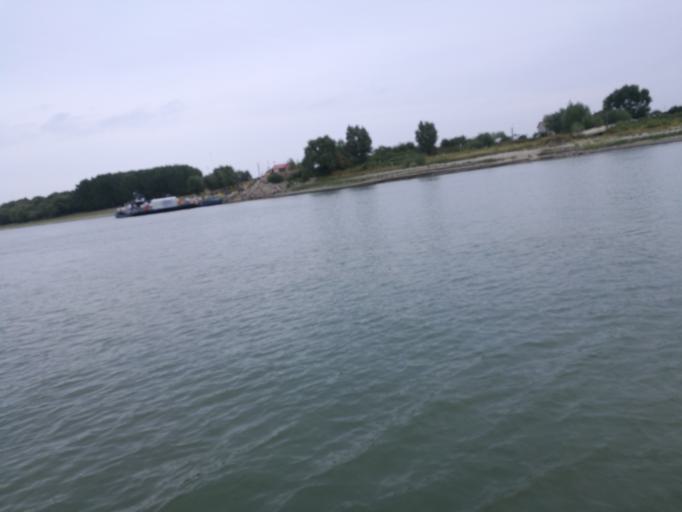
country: RO
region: Braila
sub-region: Municipiul Braila
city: Braila
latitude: 45.2874
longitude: 27.9952
